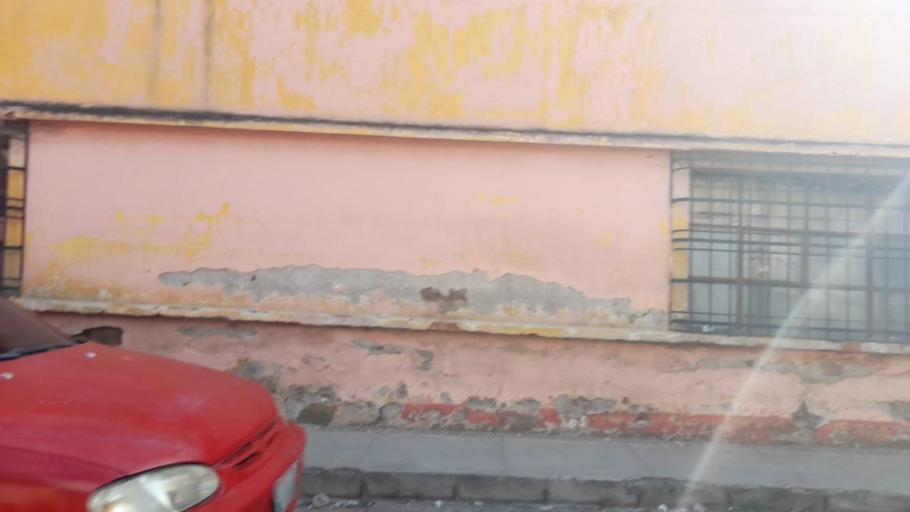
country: GT
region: Quetzaltenango
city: Quetzaltenango
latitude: 14.8374
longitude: -91.5167
